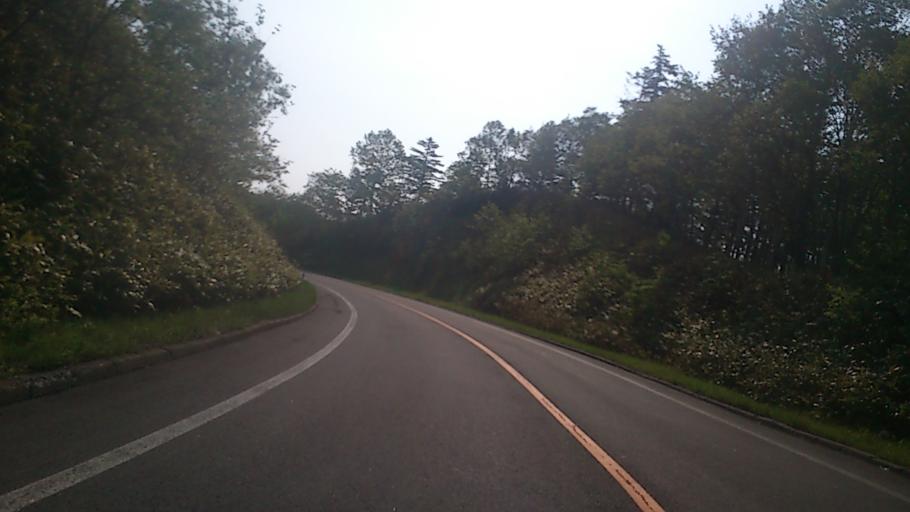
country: JP
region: Hokkaido
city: Bihoro
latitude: 43.4432
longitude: 144.1937
